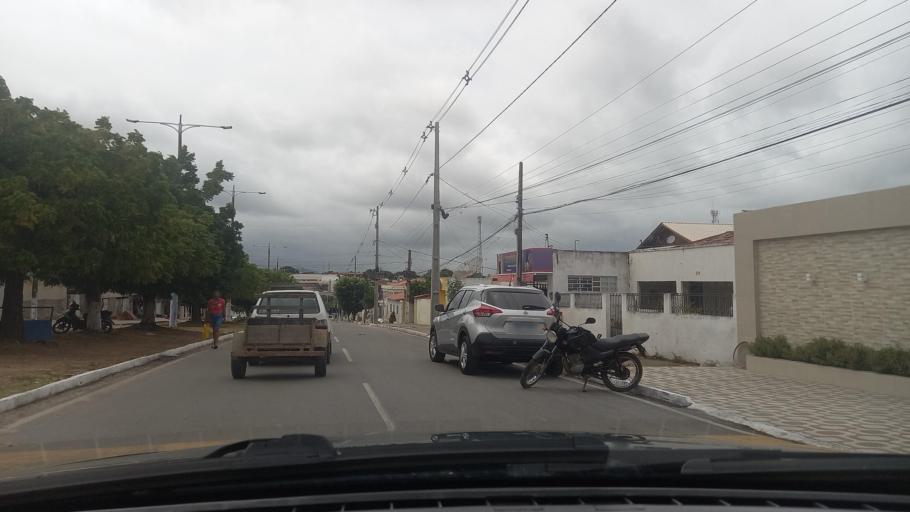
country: BR
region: Alagoas
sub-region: Delmiro Gouveia
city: Delmiro Gouveia
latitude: -9.3823
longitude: -38.0067
